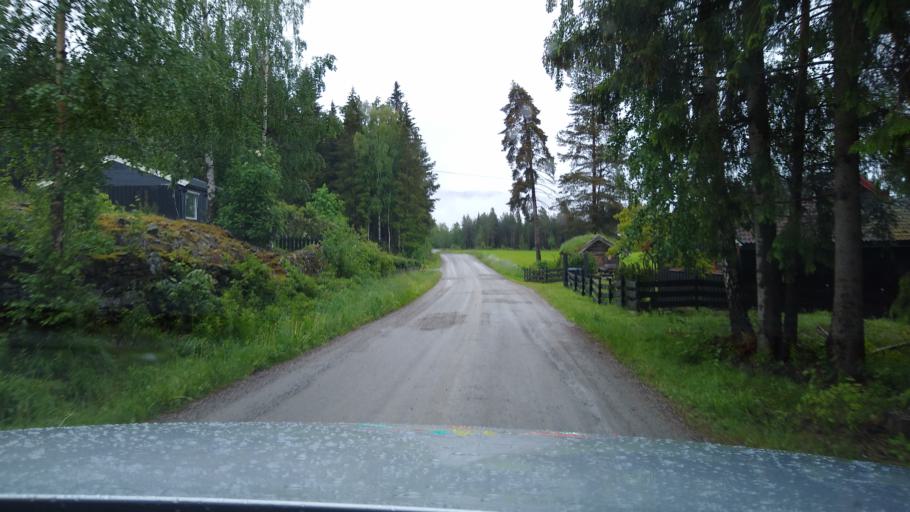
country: NO
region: Oppland
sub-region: Ringebu
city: Ringebu
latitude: 61.5404
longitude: 10.1149
